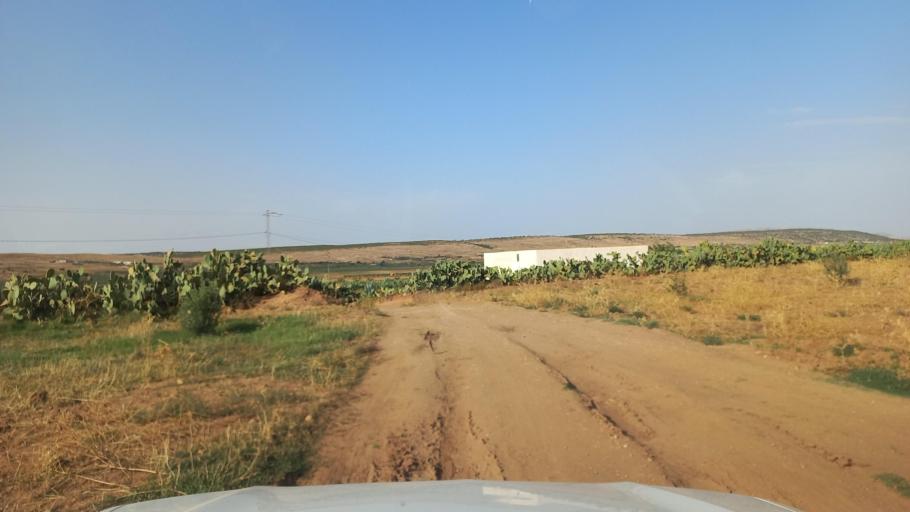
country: TN
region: Al Qasrayn
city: Kasserine
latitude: 35.3484
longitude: 8.8485
